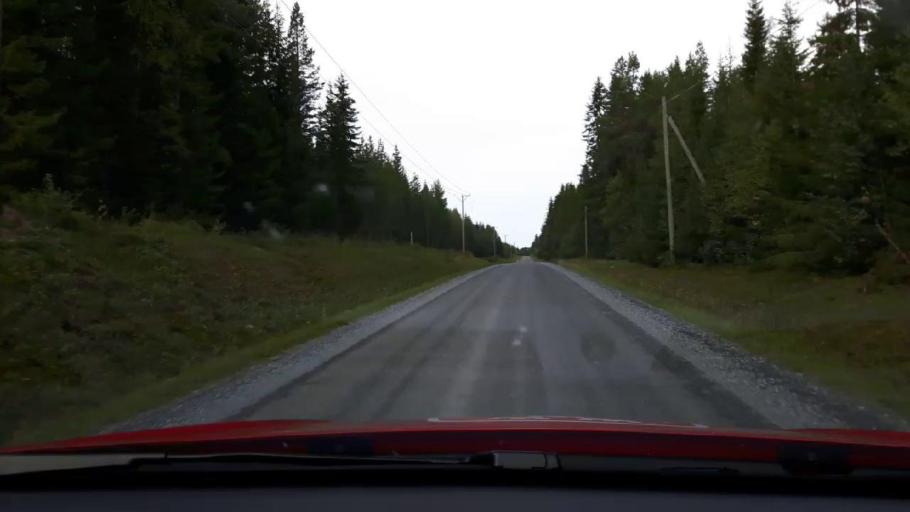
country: SE
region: Jaemtland
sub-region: Krokoms Kommun
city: Valla
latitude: 63.2469
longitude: 13.9644
